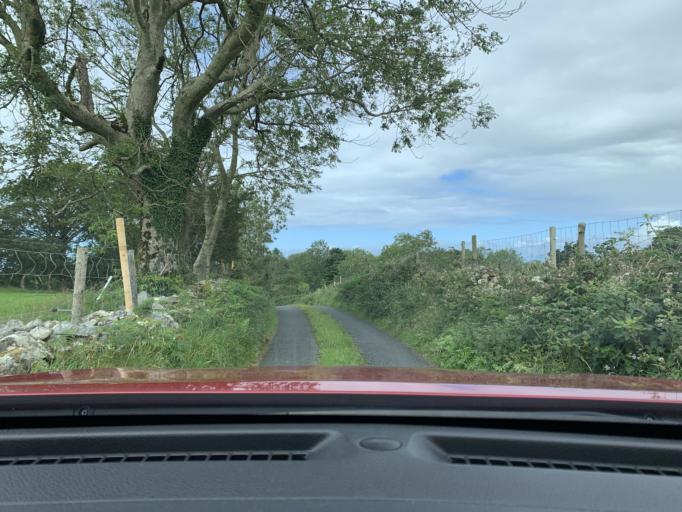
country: IE
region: Connaught
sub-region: Sligo
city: Sligo
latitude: 54.3807
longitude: -8.5065
